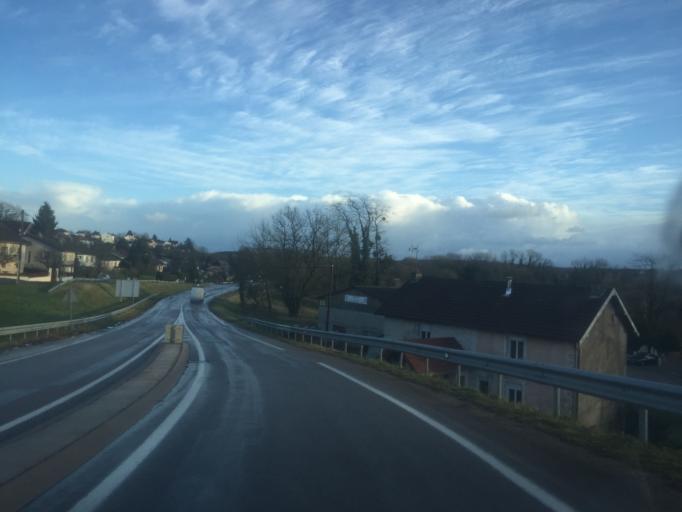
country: FR
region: Franche-Comte
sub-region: Departement du Jura
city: Dampierre
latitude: 47.1504
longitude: 5.7186
